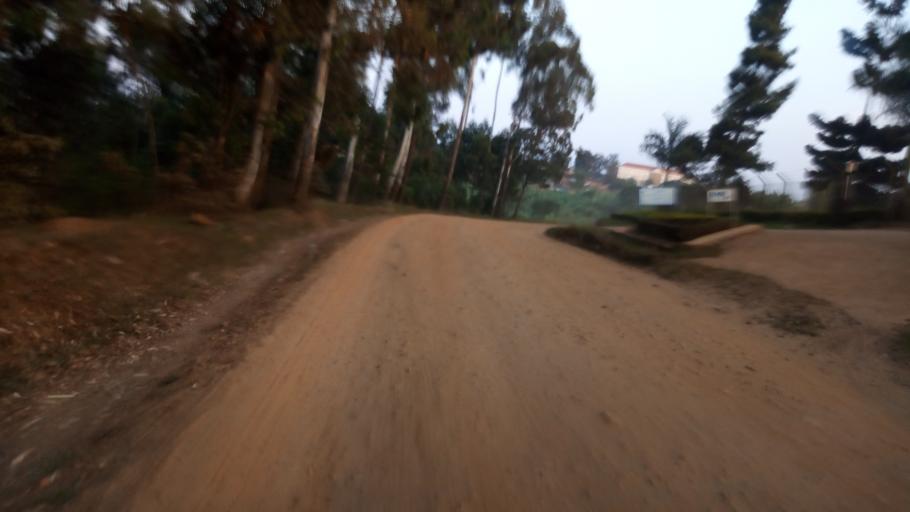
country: UG
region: Western Region
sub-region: Rukungiri District
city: Rukungiri
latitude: -0.7803
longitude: 29.9253
